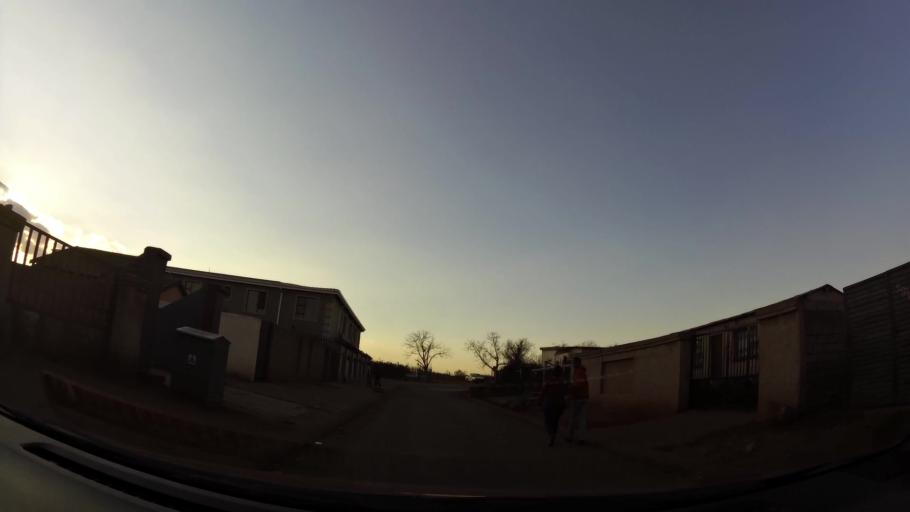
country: ZA
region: Gauteng
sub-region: City of Johannesburg Metropolitan Municipality
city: Soweto
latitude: -26.2190
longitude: 27.8567
